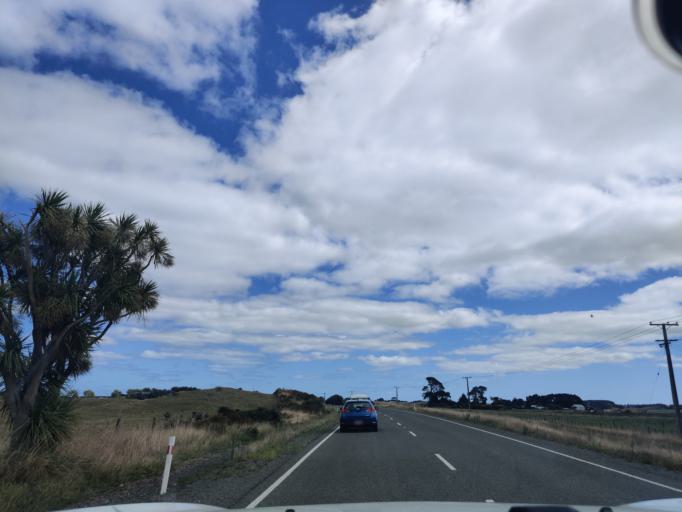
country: NZ
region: Manawatu-Wanganui
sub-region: Horowhenua District
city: Foxton
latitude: -40.4163
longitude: 175.4050
